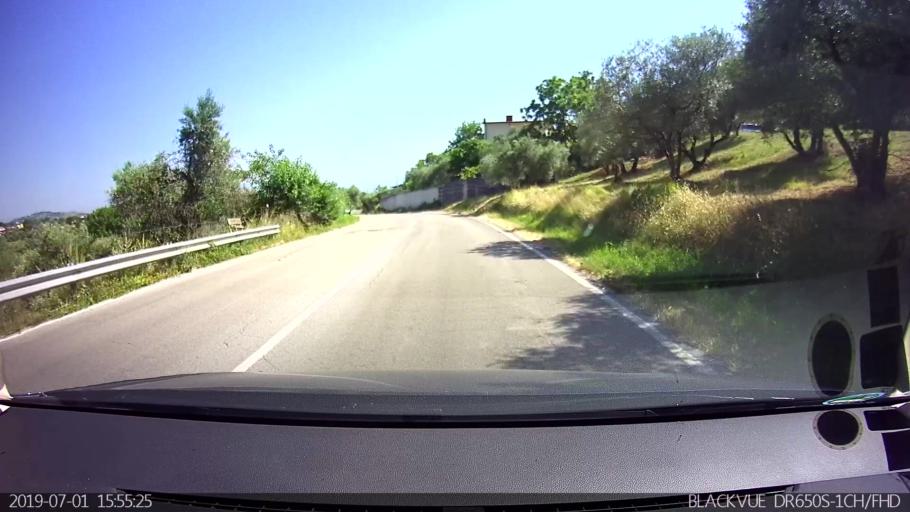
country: IT
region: Latium
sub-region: Provincia di Frosinone
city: Veroli
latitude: 41.6889
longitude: 13.4223
